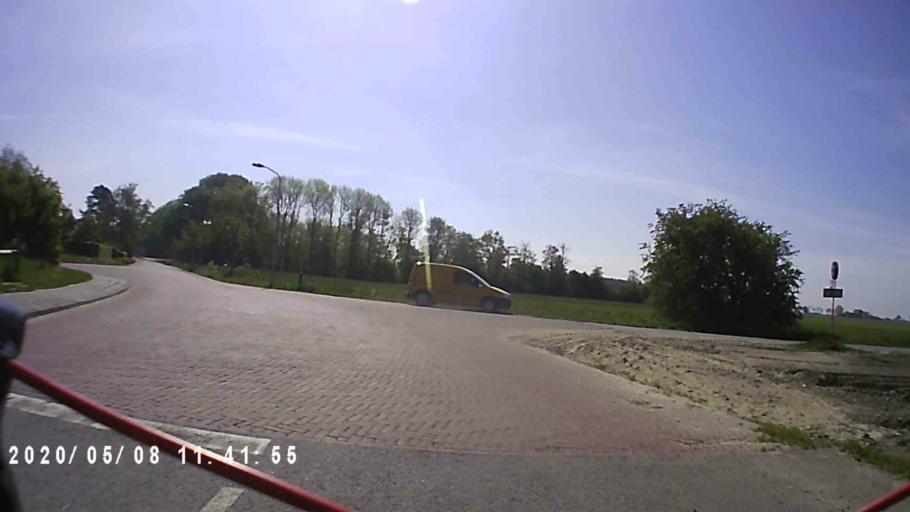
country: NL
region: Groningen
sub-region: Gemeente Bedum
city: Bedum
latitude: 53.3260
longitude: 6.6857
